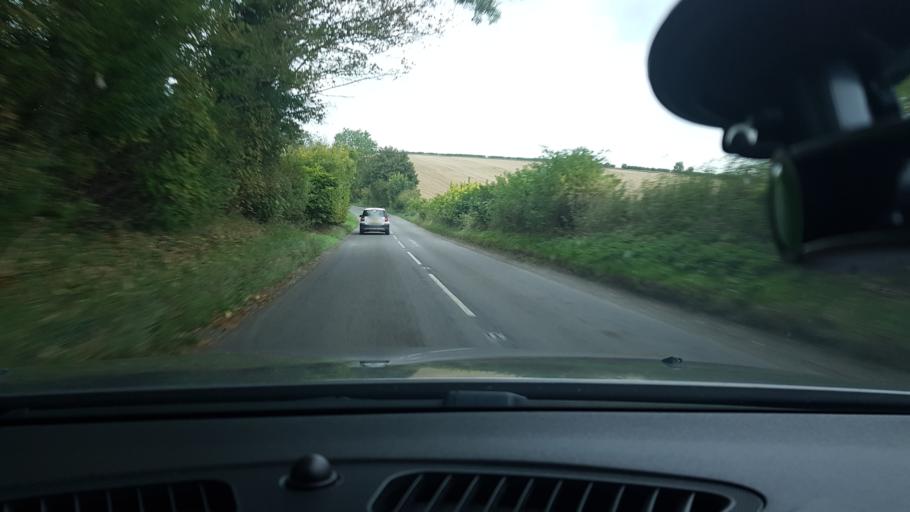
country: GB
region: England
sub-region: Wiltshire
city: Shalbourne
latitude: 51.3563
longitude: -1.5759
